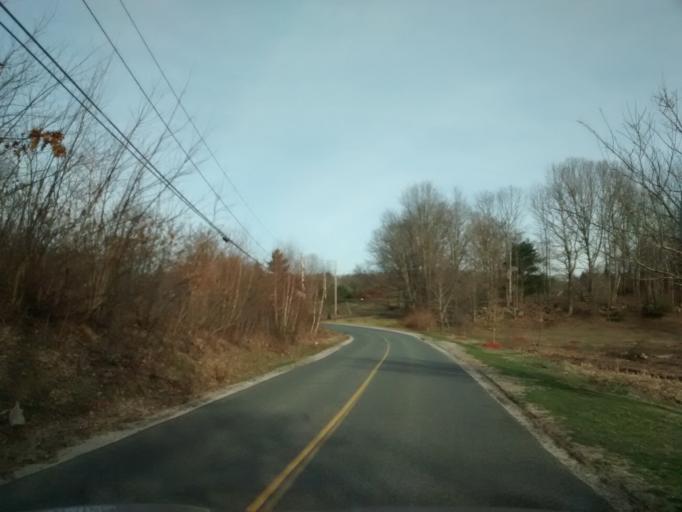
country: US
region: Massachusetts
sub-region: Worcester County
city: Charlton
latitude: 42.1248
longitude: -72.0100
